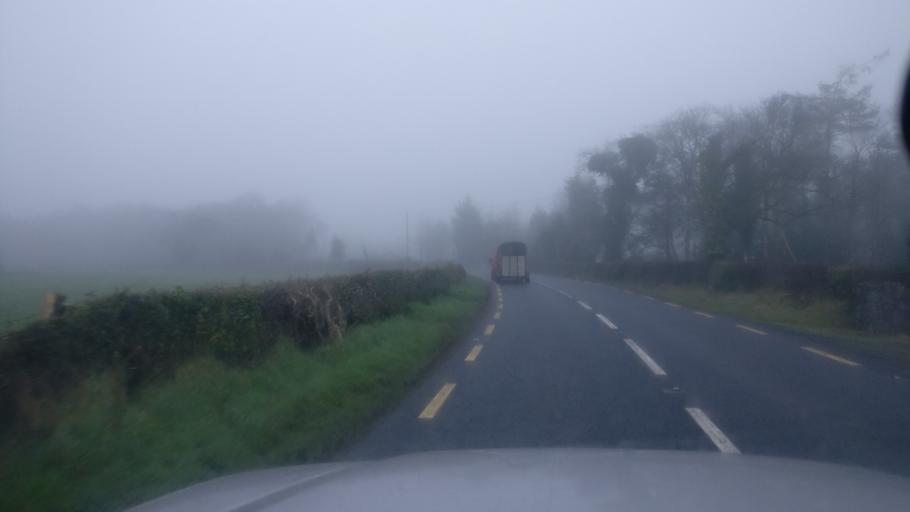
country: IE
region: Connaught
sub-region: County Galway
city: Loughrea
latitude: 53.1459
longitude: -8.6950
